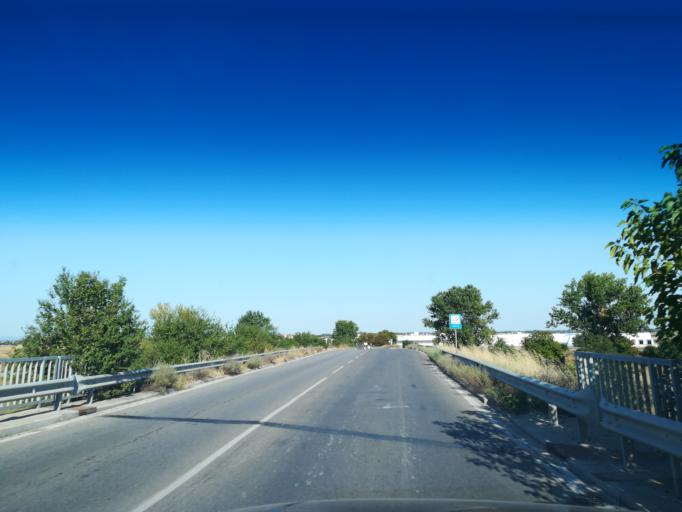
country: BG
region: Plovdiv
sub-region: Obshtina Plovdiv
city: Plovdiv
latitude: 42.1727
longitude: 24.8201
